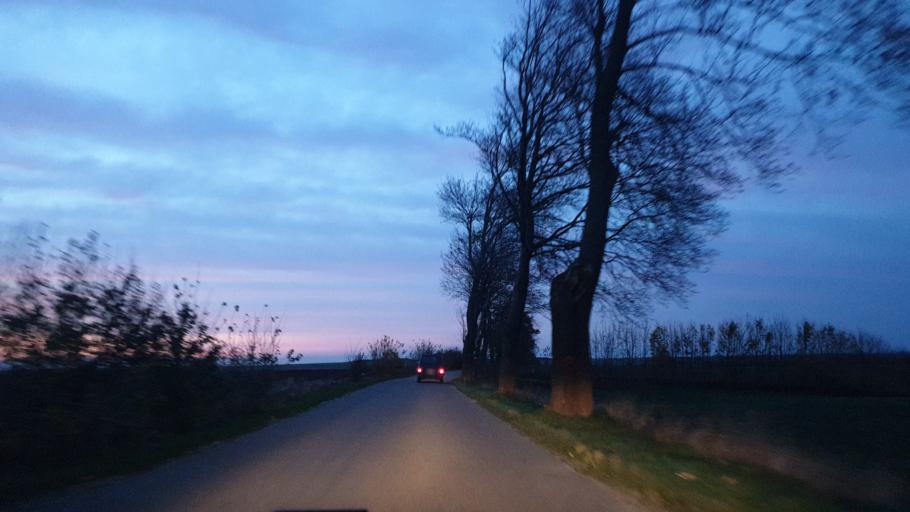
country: PL
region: Pomeranian Voivodeship
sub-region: Powiat pucki
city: Krokowa
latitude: 54.7783
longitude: 18.2054
